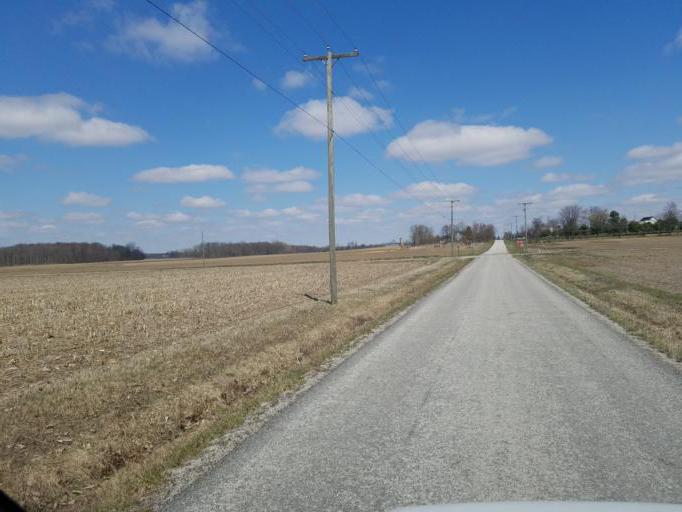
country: US
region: Ohio
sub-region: Crawford County
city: Galion
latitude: 40.7113
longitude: -82.8494
